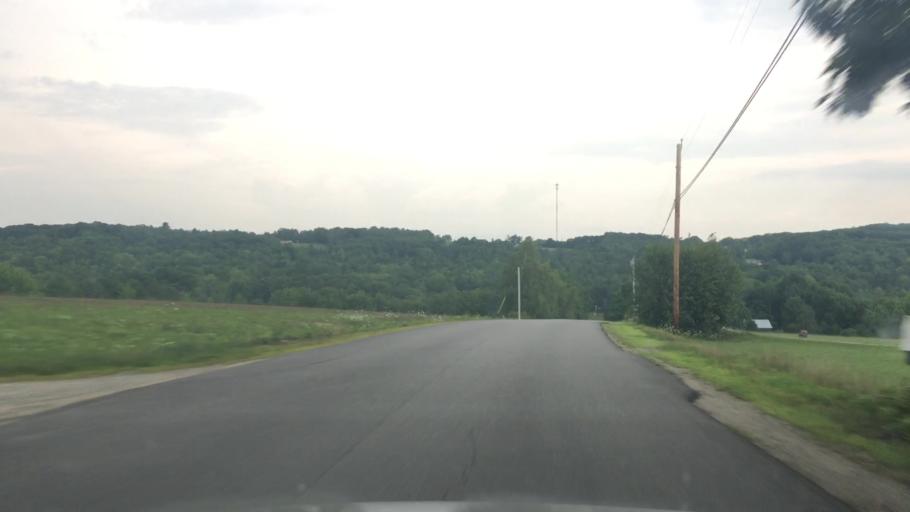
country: US
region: Maine
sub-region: Knox County
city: Washington
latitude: 44.3836
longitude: -69.3554
